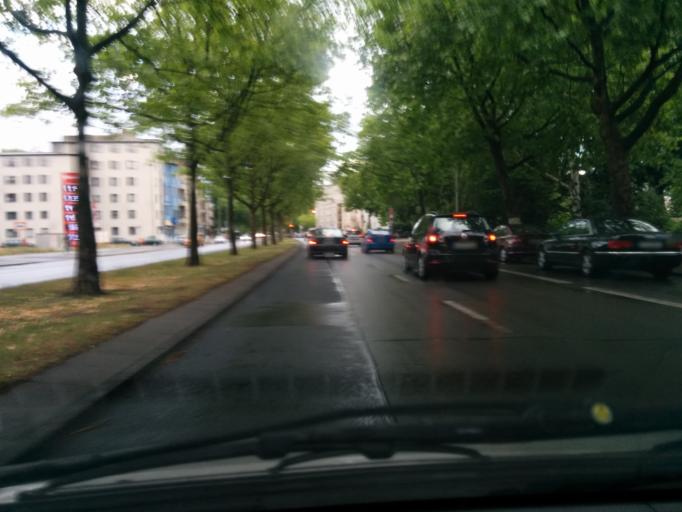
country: DE
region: Berlin
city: Spandau
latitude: 52.5294
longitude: 13.2062
